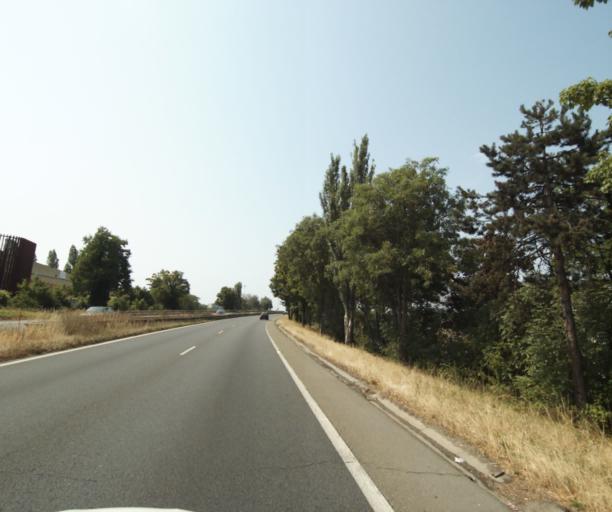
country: FR
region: Ile-de-France
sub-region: Departement du Val-d'Oise
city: Eragny
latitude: 49.0111
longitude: 2.0889
